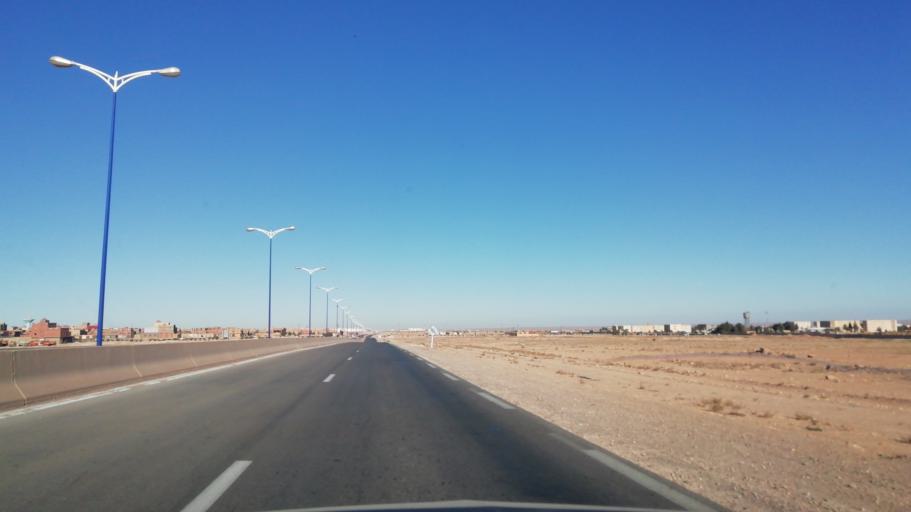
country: DZ
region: Wilaya de Naama
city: Naama
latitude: 33.5313
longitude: -0.2702
